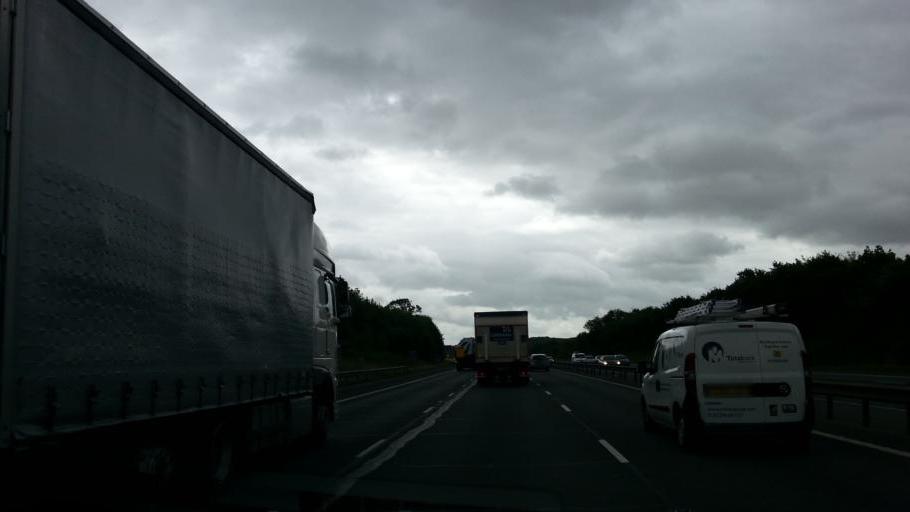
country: GB
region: England
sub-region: Warwickshire
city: Harbury
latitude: 52.2225
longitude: -1.5128
